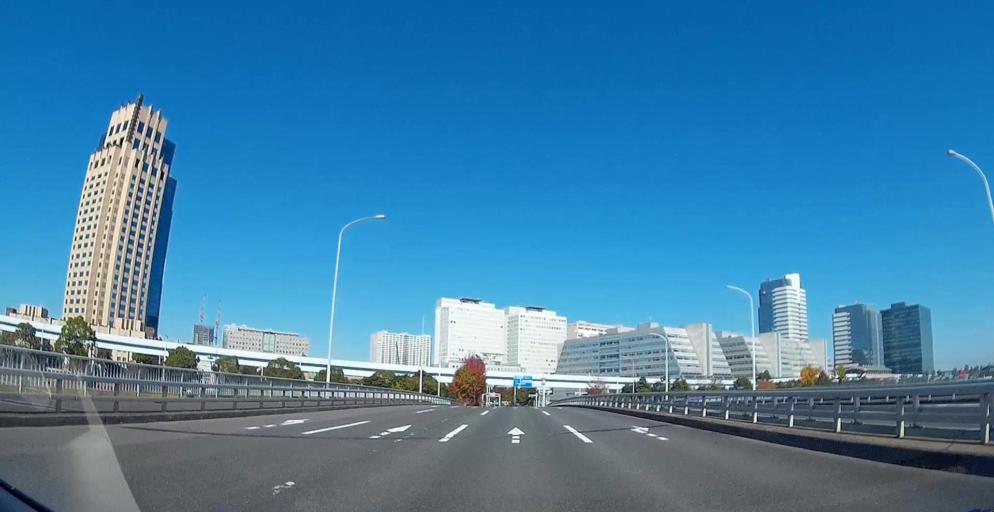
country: JP
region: Tokyo
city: Urayasu
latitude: 35.6272
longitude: 139.7890
